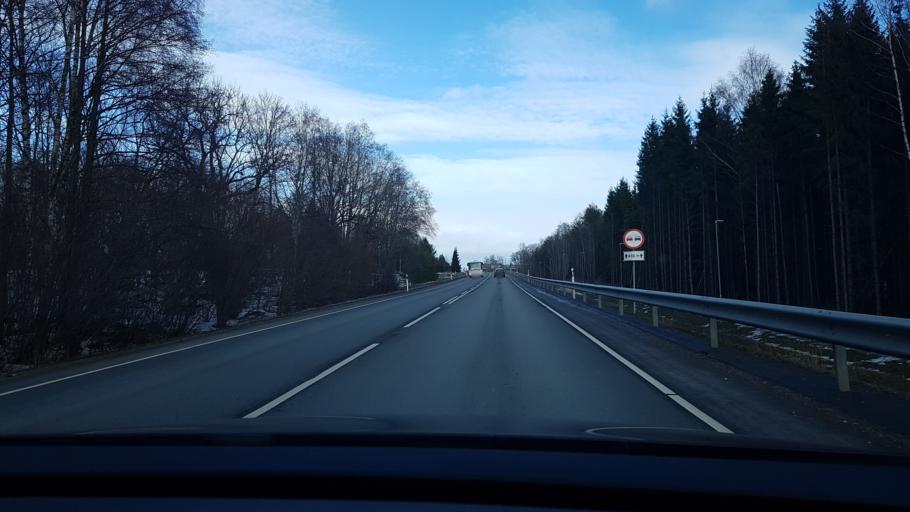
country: EE
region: Paernumaa
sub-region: Tootsi vald
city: Tootsi
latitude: 58.5127
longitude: 24.8130
